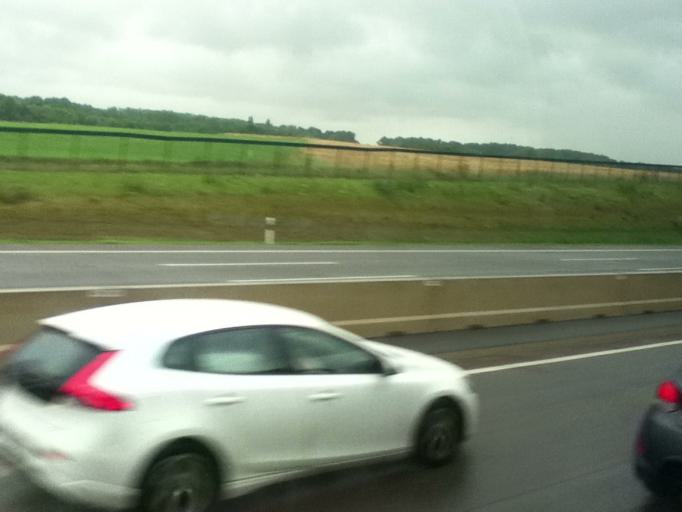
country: DE
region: Thuringia
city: Bischofroda
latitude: 50.9974
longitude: 10.4163
